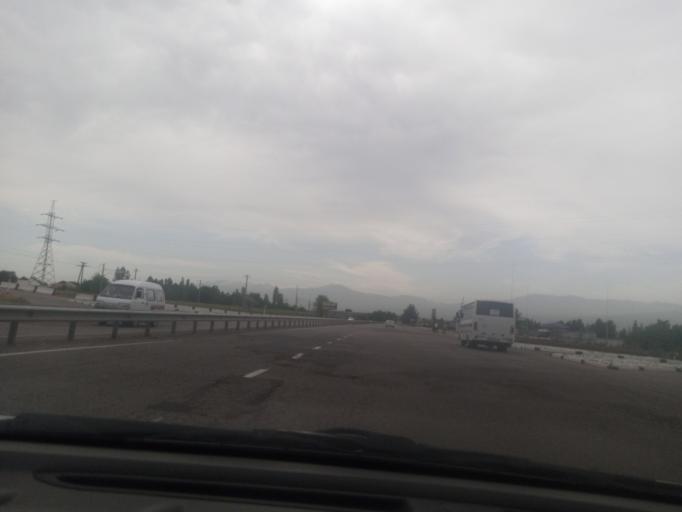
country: UZ
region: Toshkent
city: Ohangaron
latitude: 40.9091
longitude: 69.7906
